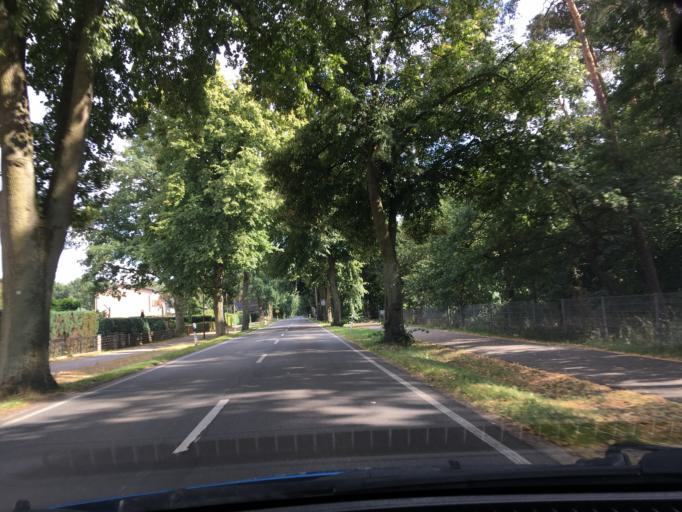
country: DE
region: Mecklenburg-Vorpommern
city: Lubtheen
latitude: 53.2954
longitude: 11.0868
